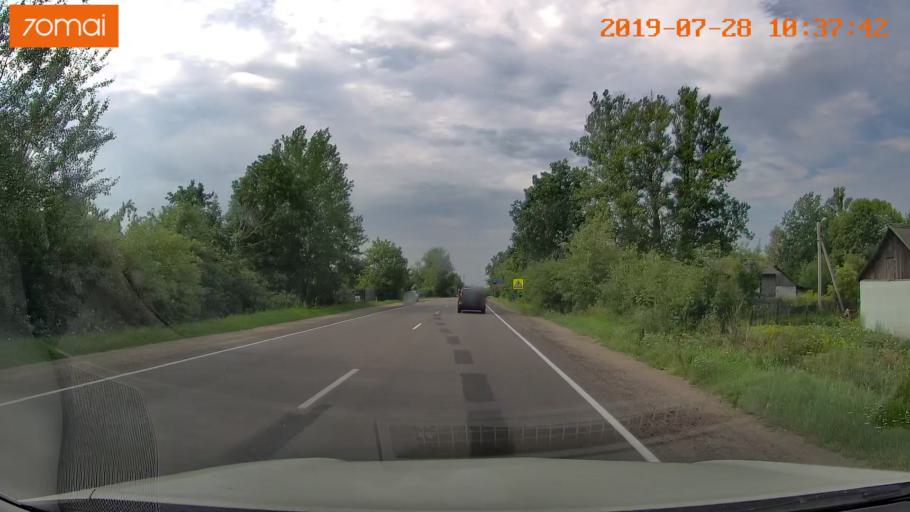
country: RU
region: Kaliningrad
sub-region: Gorod Kaliningrad
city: Kaliningrad
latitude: 54.7291
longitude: 20.4058
